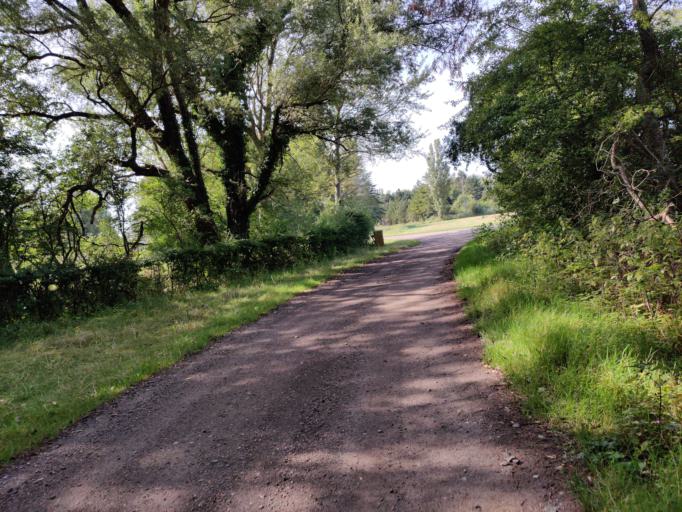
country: DK
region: Zealand
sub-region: Guldborgsund Kommune
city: Nykobing Falster
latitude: 54.6028
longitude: 11.9474
